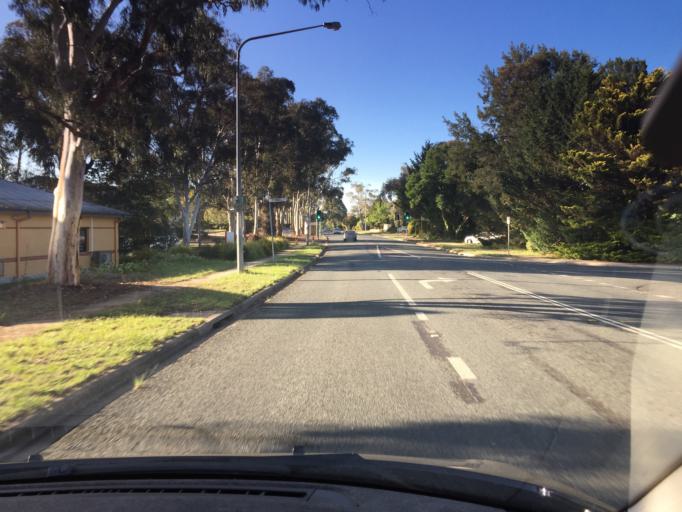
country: AU
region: Australian Capital Territory
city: Kaleen
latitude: -35.2232
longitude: 149.1110
